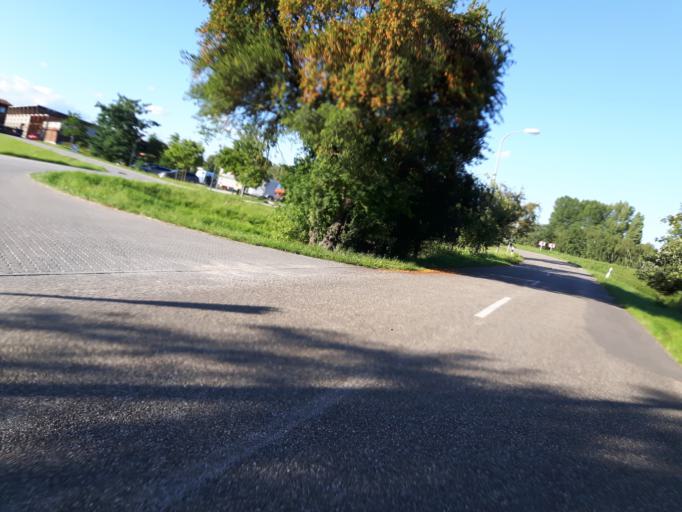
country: DE
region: Baden-Wuerttemberg
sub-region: Karlsruhe Region
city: Bruhl
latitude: 49.3891
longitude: 8.4954
